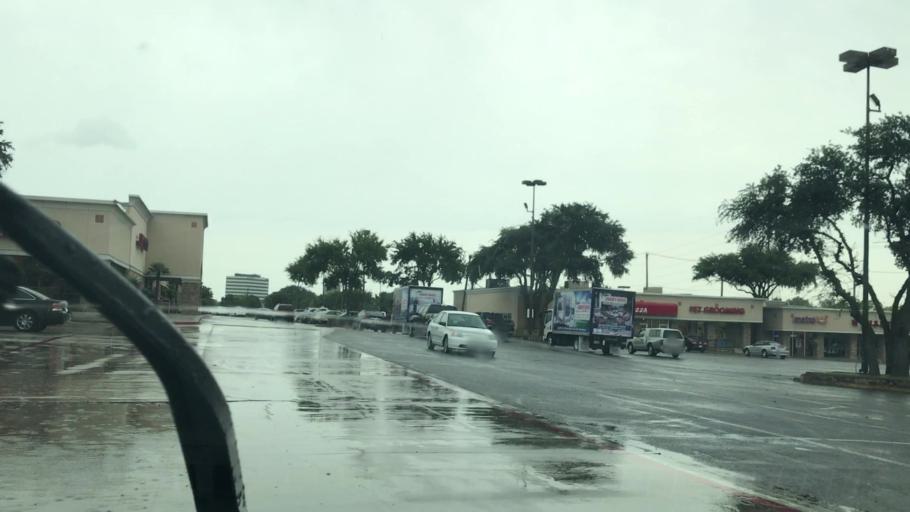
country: US
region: Texas
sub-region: Dallas County
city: Richardson
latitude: 32.9404
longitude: -96.7703
